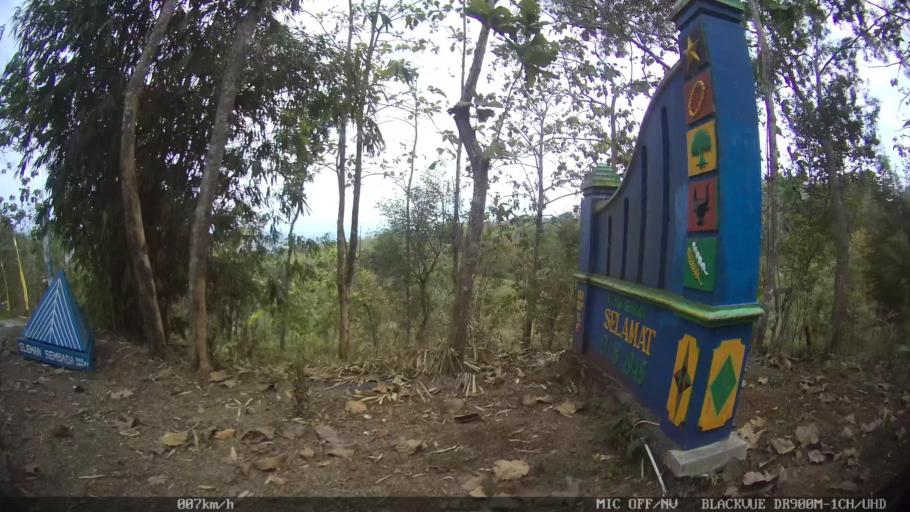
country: ID
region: Central Java
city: Candi Prambanan
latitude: -7.7988
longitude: 110.5208
